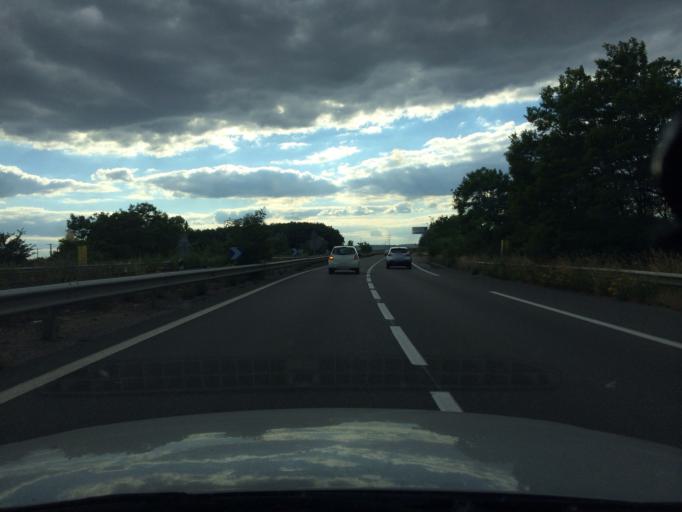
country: FR
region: Lorraine
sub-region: Departement de Meurthe-et-Moselle
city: Saint-Nicolas-de-Port
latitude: 48.6169
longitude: 6.2817
